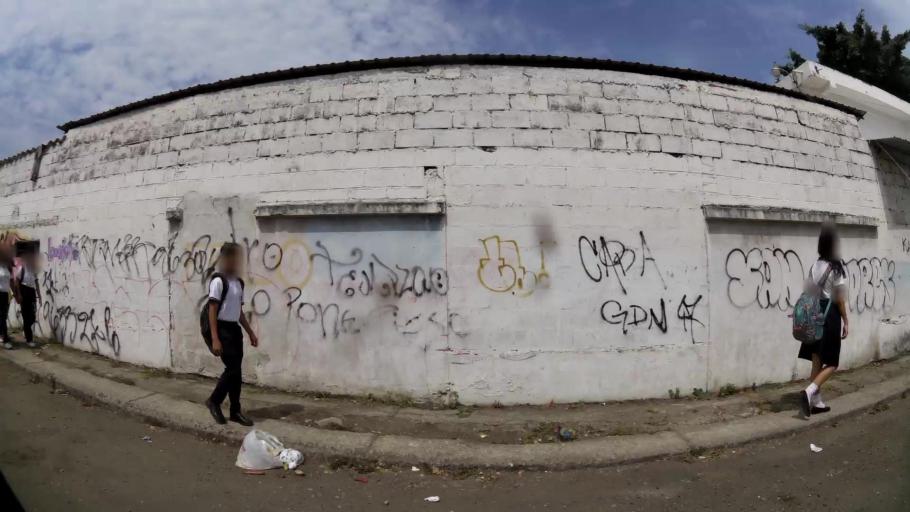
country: EC
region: Guayas
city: Eloy Alfaro
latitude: -2.1429
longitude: -79.8993
